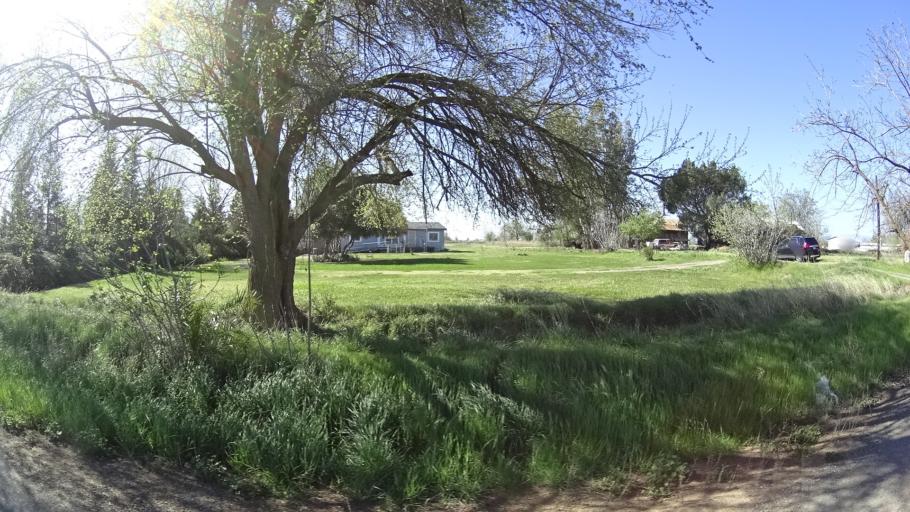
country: US
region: California
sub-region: Glenn County
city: Orland
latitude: 39.7369
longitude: -122.2274
